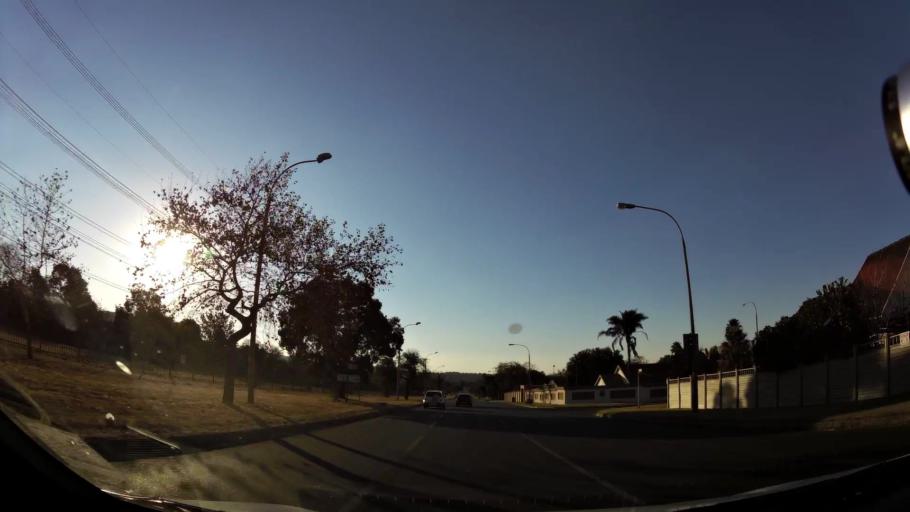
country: ZA
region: Gauteng
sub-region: Ekurhuleni Metropolitan Municipality
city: Germiston
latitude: -26.2803
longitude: 28.1103
